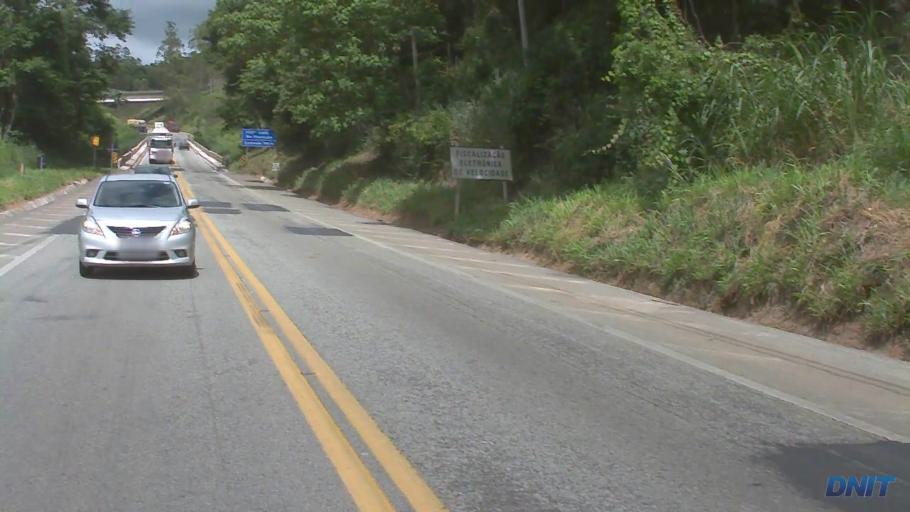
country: BR
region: Minas Gerais
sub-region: Joao Monlevade
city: Joao Monlevade
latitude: -19.8522
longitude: -43.1391
